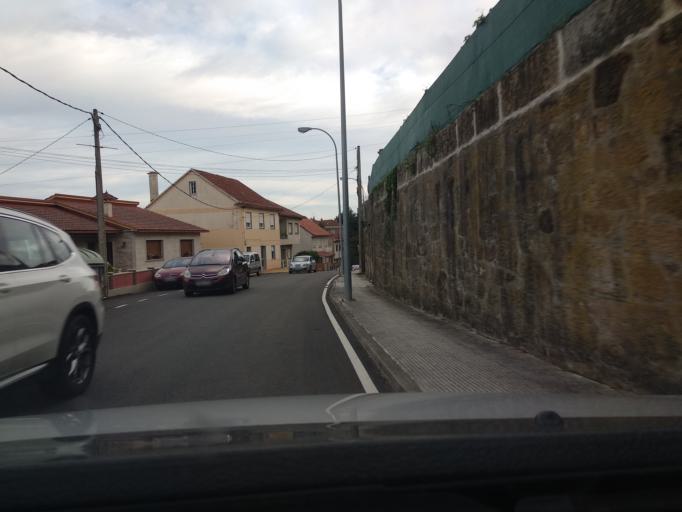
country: ES
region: Galicia
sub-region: Provincia de Pontevedra
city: Moana
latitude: 42.2915
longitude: -8.7384
